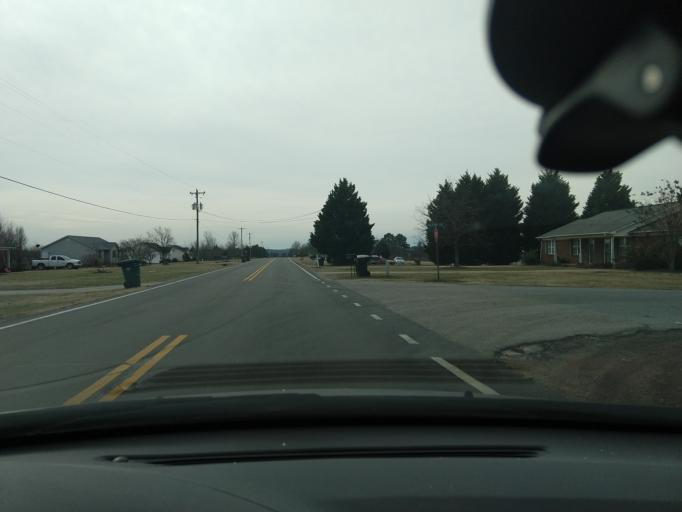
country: US
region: South Carolina
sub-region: Spartanburg County
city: Cowpens
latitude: 35.0531
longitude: -81.7874
